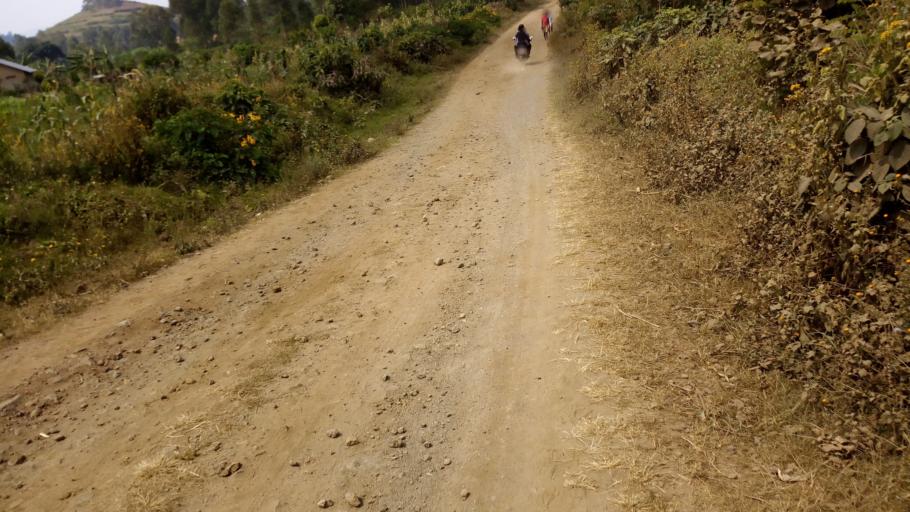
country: UG
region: Western Region
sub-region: Kisoro District
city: Kisoro
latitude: -1.3149
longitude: 29.7181
